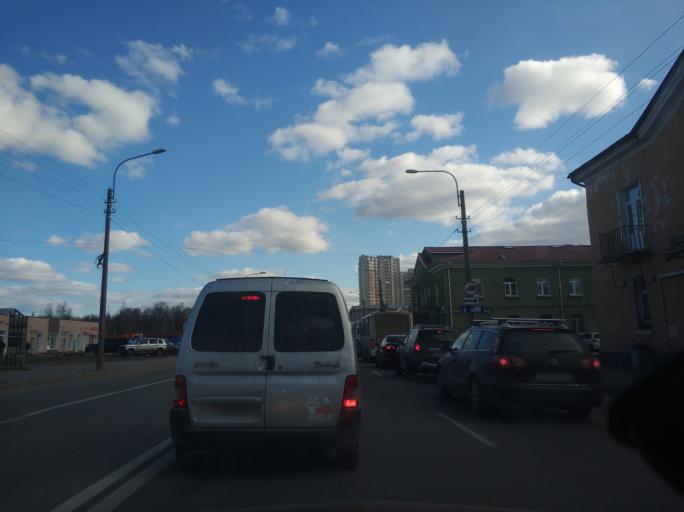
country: RU
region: St.-Petersburg
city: Krasnogvargeisky
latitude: 59.9634
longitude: 30.4871
